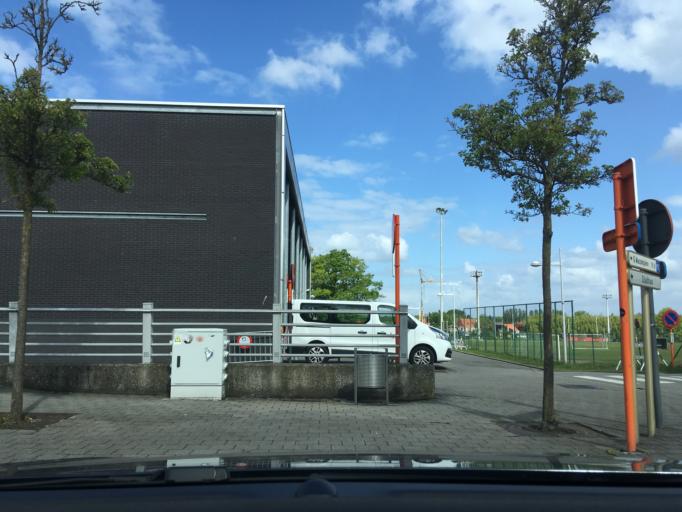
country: BE
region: Flanders
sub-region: Provincie West-Vlaanderen
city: Tielt
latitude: 51.0023
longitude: 3.3282
